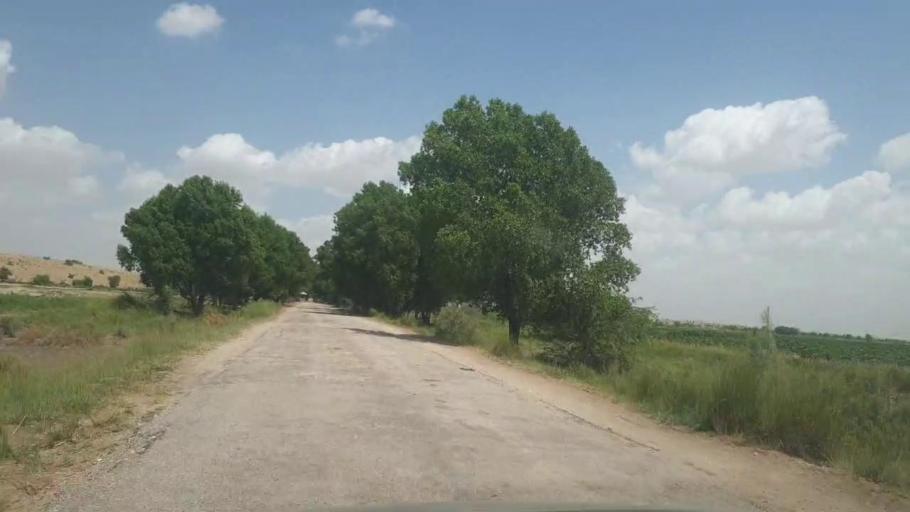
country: PK
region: Sindh
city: Kot Diji
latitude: 27.2198
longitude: 69.0468
